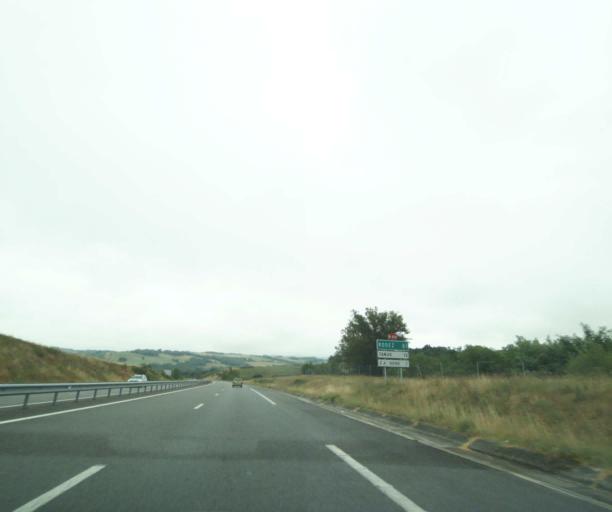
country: FR
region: Midi-Pyrenees
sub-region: Departement du Tarn
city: Le Garric
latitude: 44.0345
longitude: 2.2004
